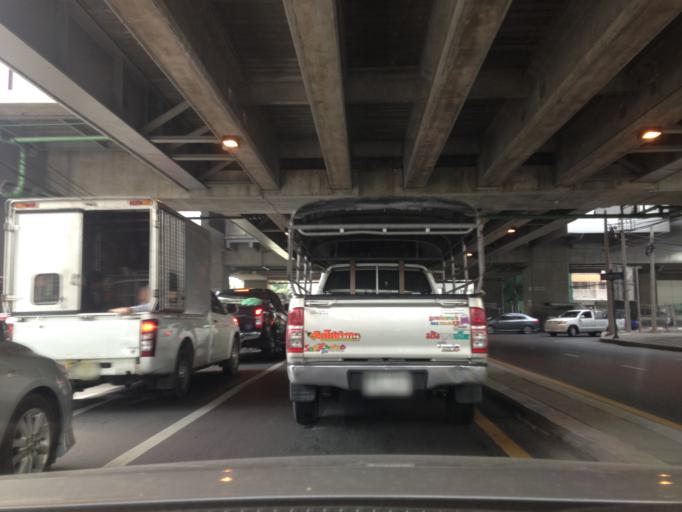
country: TH
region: Bangkok
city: Bang Sue
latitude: 13.8068
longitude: 100.5309
